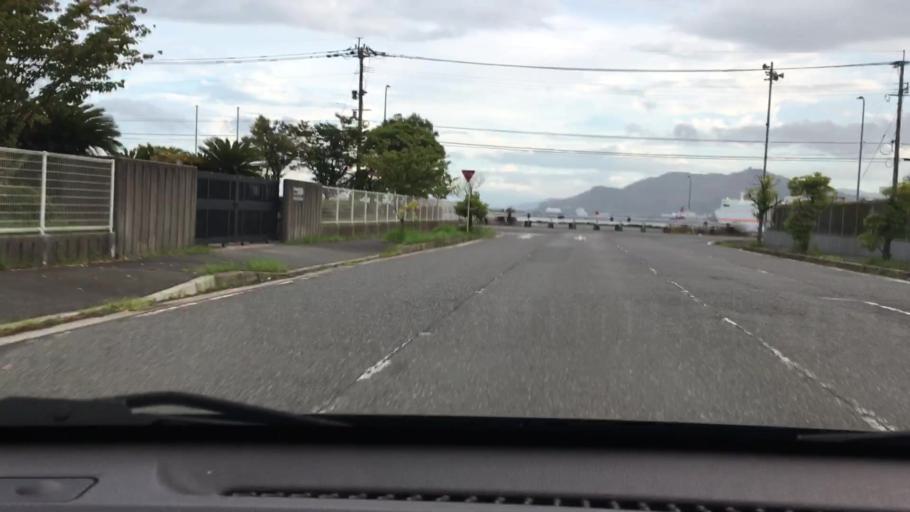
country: JP
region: Yamaguchi
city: Shimonoseki
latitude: 33.8869
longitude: 130.9927
